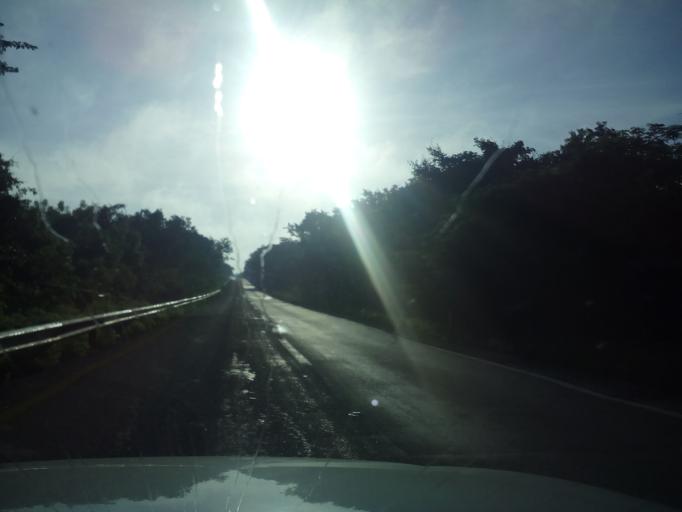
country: MX
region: Yucatan
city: Tunkas
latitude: 20.7637
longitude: -88.7925
